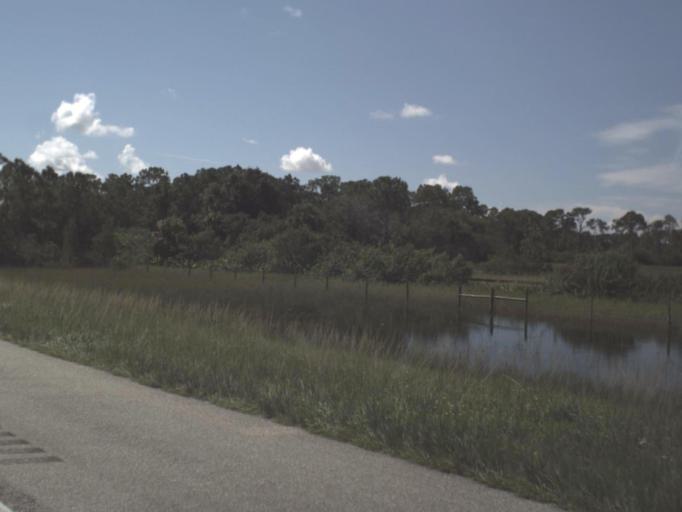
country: US
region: Florida
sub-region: Lee County
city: Suncoast Estates
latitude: 26.8079
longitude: -81.9290
